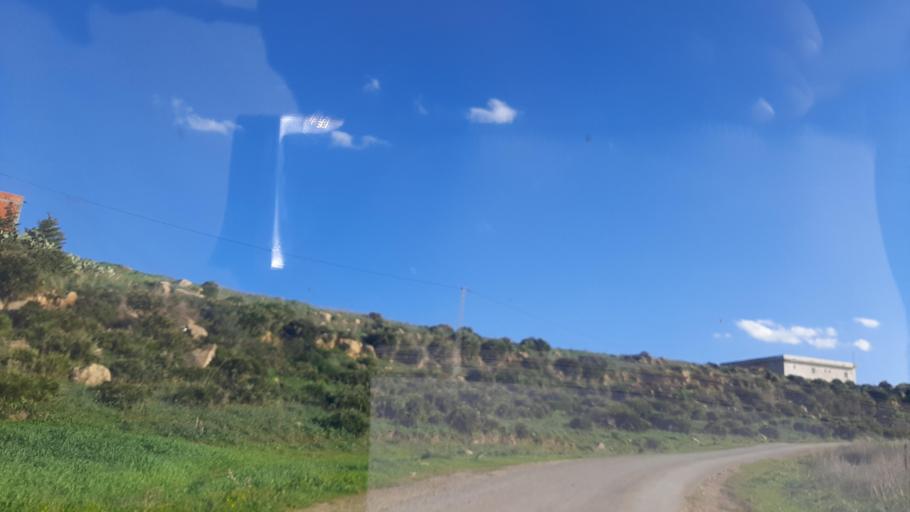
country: TN
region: Nabul
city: El Mida
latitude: 36.8101
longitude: 10.8455
